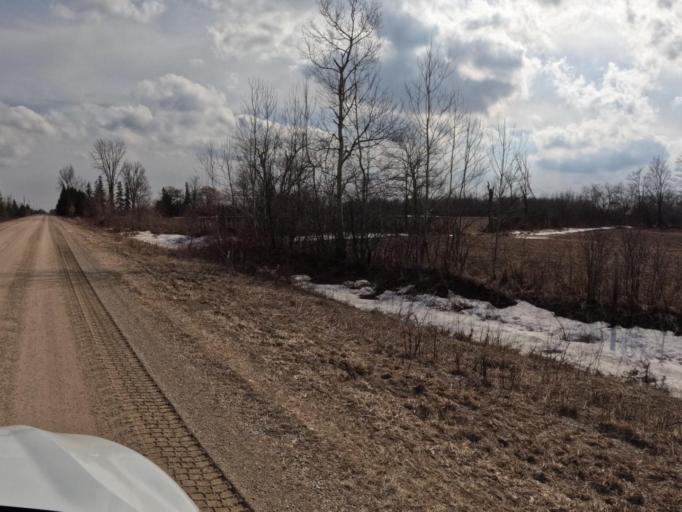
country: CA
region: Ontario
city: Shelburne
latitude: 43.9364
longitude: -80.3098
